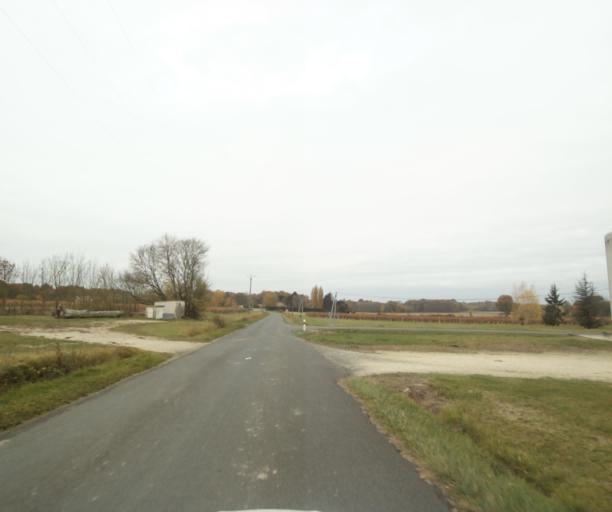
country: FR
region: Poitou-Charentes
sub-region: Departement de la Charente-Maritime
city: Chermignac
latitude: 45.7195
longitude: -0.6933
